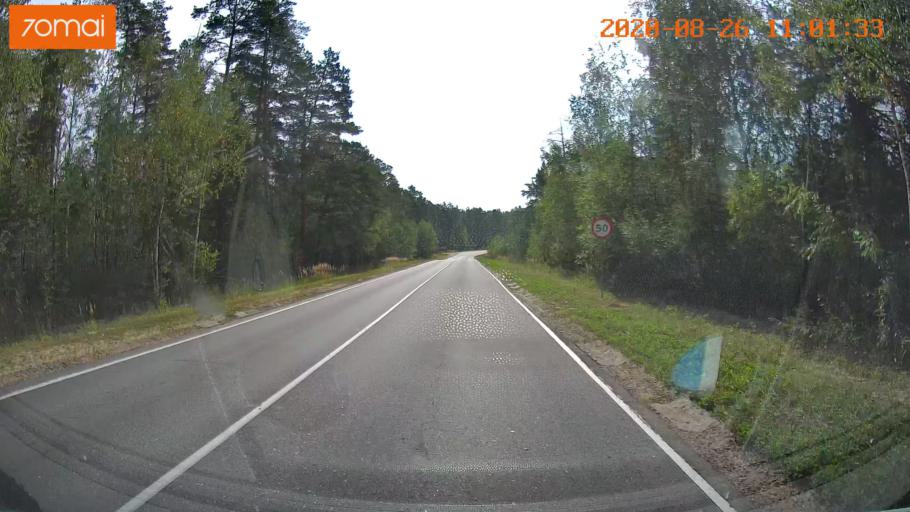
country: RU
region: Rjazan
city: Izhevskoye
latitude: 54.5617
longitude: 41.2257
